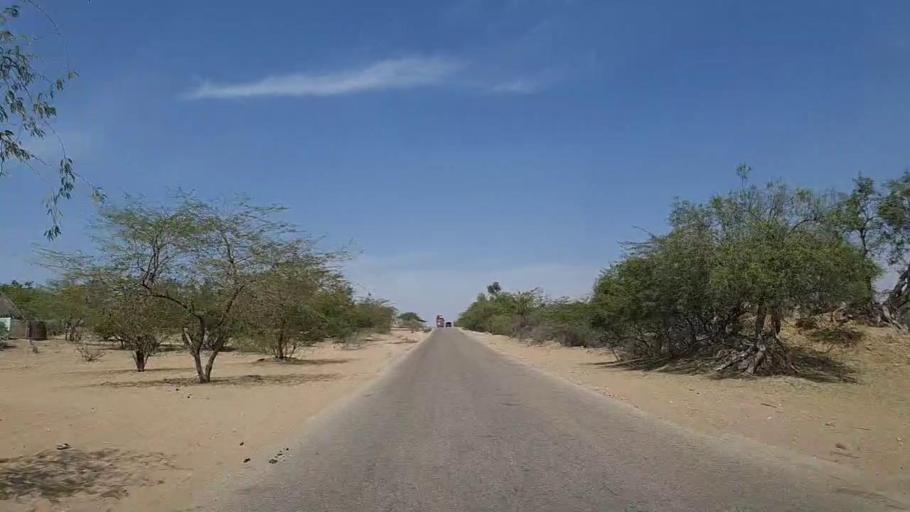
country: PK
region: Sindh
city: Mithi
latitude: 24.9873
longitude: 69.9225
